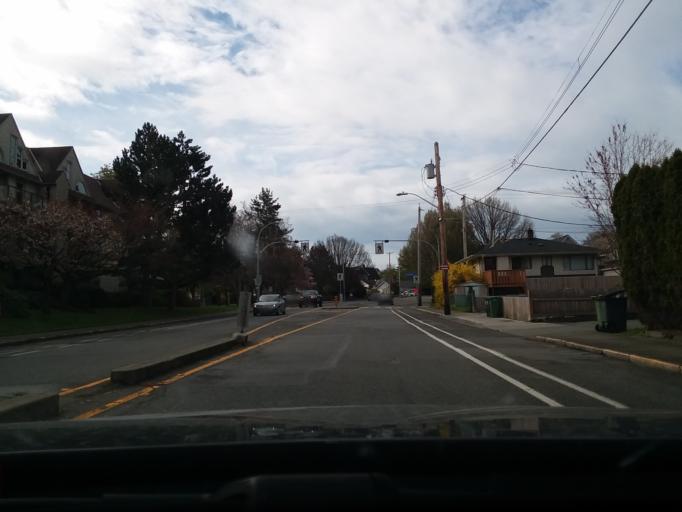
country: CA
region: British Columbia
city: Oak Bay
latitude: 48.4317
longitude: -123.3330
